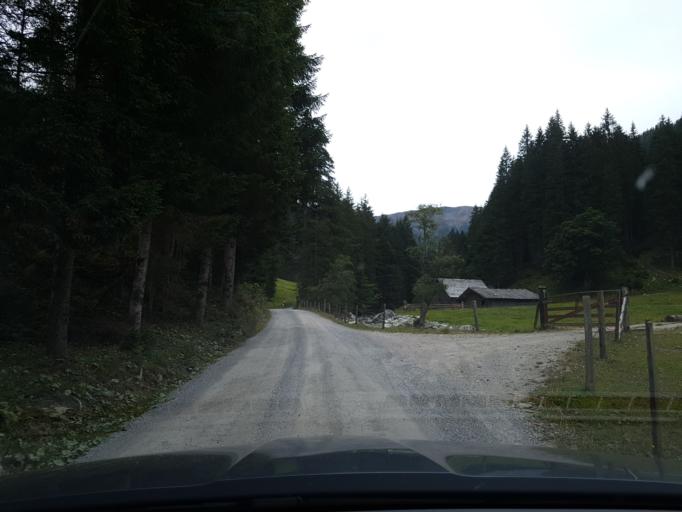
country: AT
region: Salzburg
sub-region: Politischer Bezirk Sankt Johann im Pongau
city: Forstau
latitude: 47.3195
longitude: 13.5793
